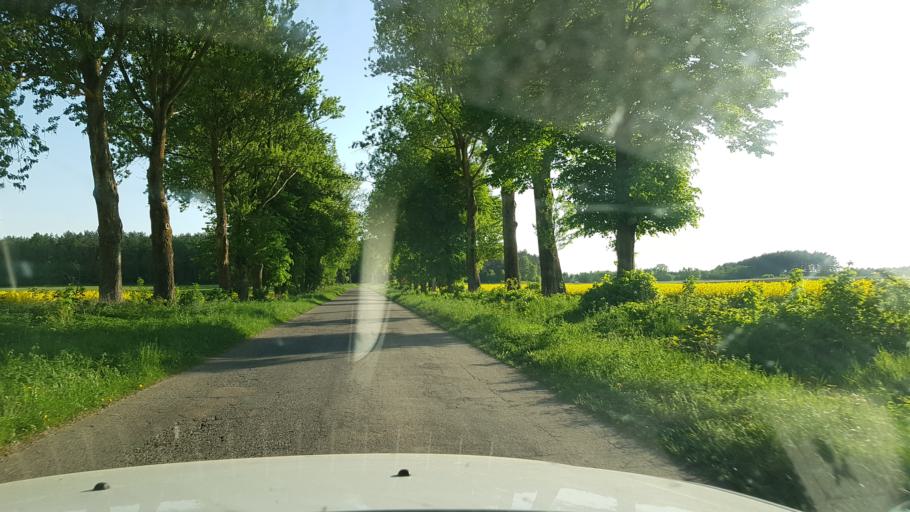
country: PL
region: West Pomeranian Voivodeship
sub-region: Powiat lobeski
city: Dobra
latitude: 53.6244
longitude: 15.3521
